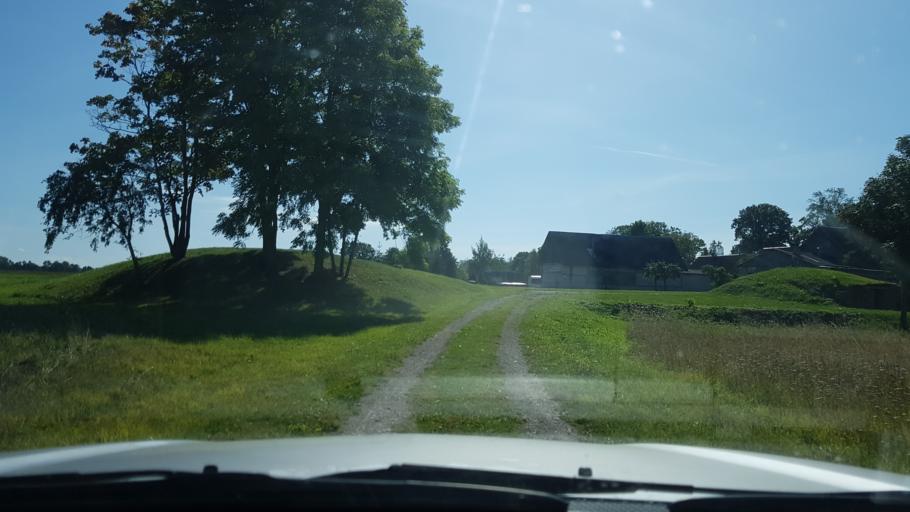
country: EE
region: Ida-Virumaa
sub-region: Sillamaee linn
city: Sillamae
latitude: 59.3913
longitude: 27.8152
